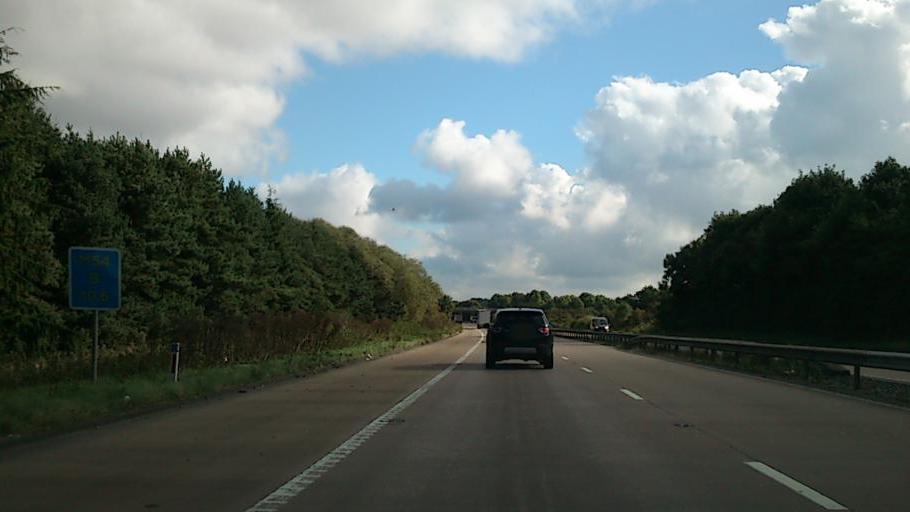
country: GB
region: England
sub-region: Staffordshire
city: Codsall
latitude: 52.6440
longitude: -2.1969
